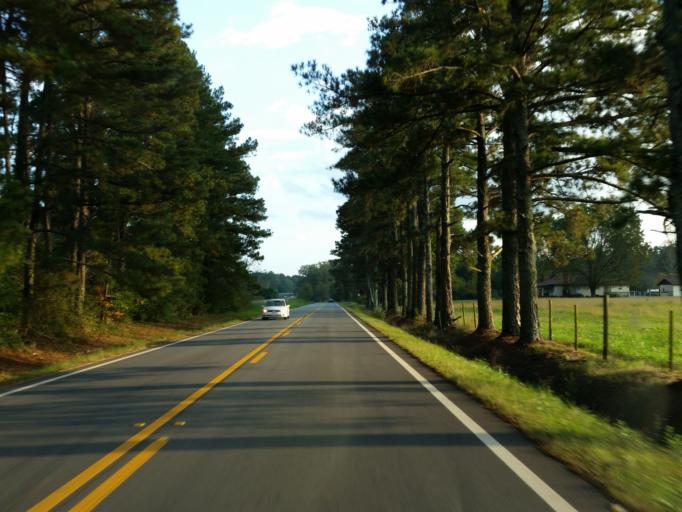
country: US
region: Georgia
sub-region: Monroe County
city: Forsyth
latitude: 32.9764
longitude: -83.8727
